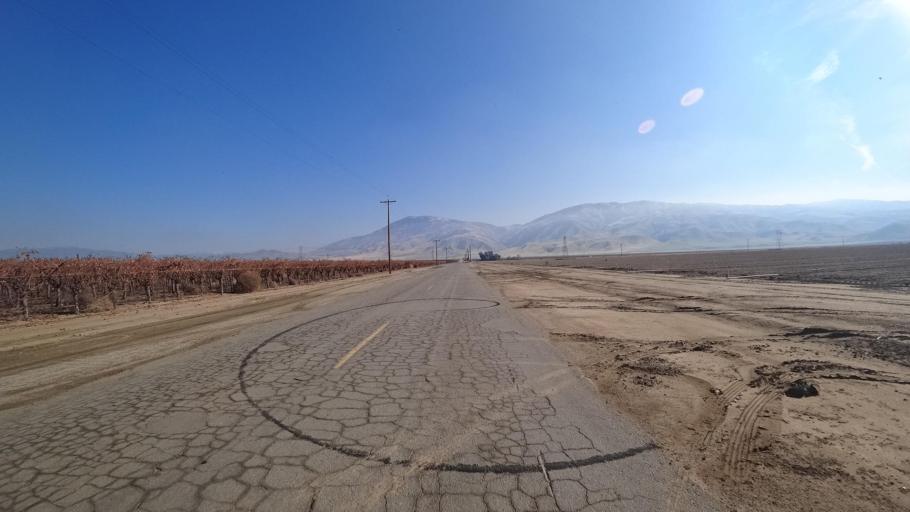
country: US
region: California
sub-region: Kern County
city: Arvin
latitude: 35.1941
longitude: -118.8097
